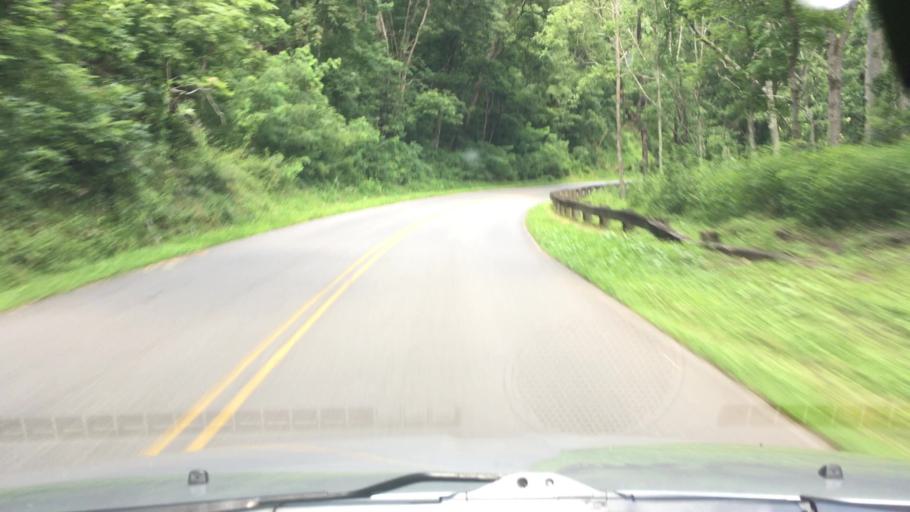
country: US
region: North Carolina
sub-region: Buncombe County
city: Weaverville
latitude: 35.6664
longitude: -82.4757
